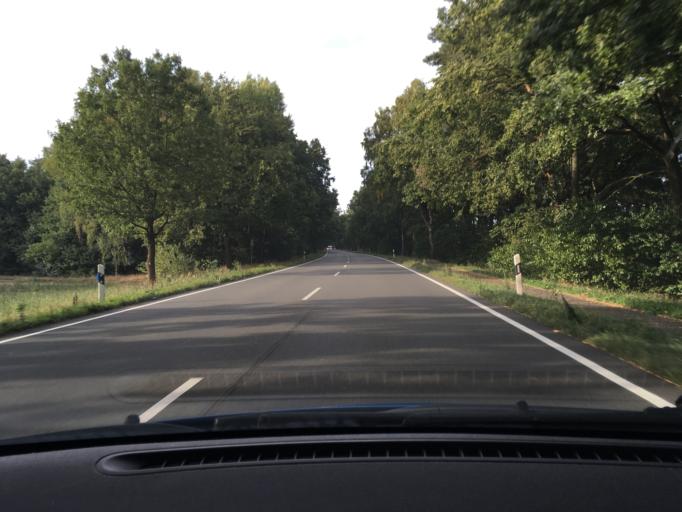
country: DE
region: Lower Saxony
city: Wietzendorf
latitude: 52.9031
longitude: 9.9189
